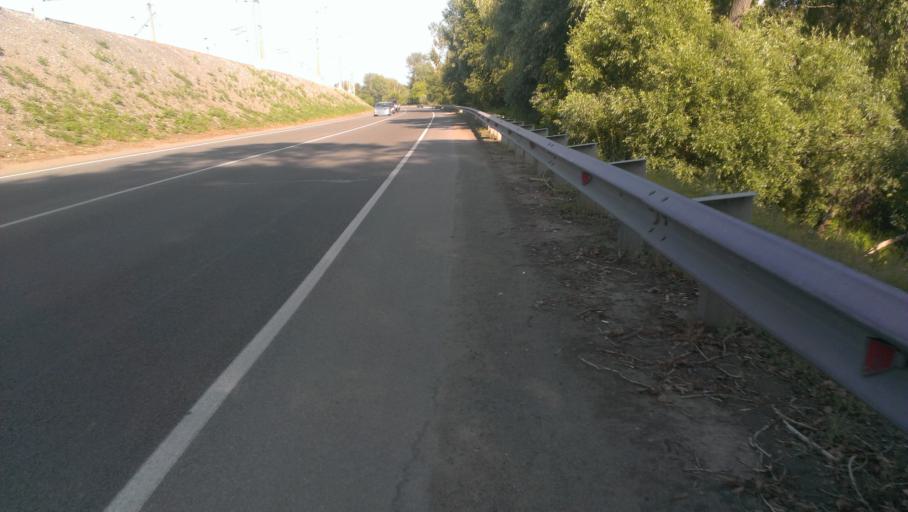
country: RU
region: Altai Krai
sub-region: Gorod Barnaulskiy
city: Barnaul
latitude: 53.3670
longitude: 83.8386
